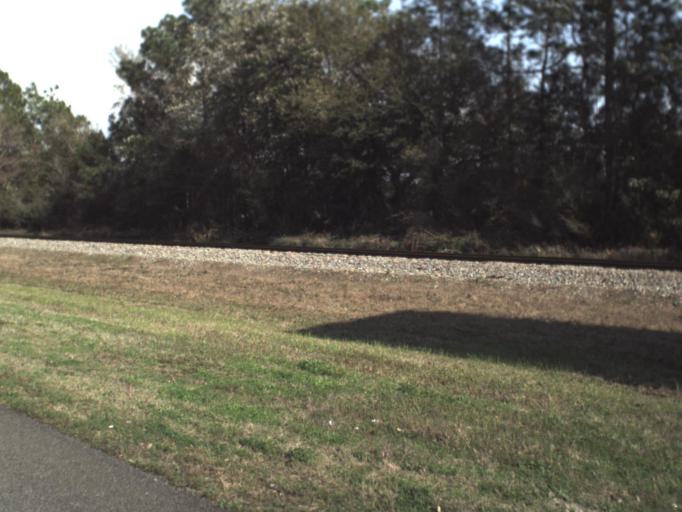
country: US
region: Florida
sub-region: Bay County
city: Hiland Park
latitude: 30.2439
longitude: -85.5638
